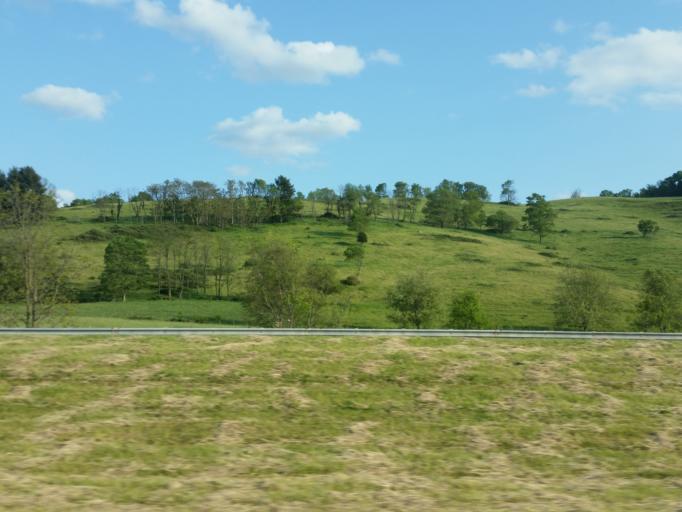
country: US
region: Virginia
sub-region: Russell County
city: Honaker
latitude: 36.9722
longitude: -81.8974
